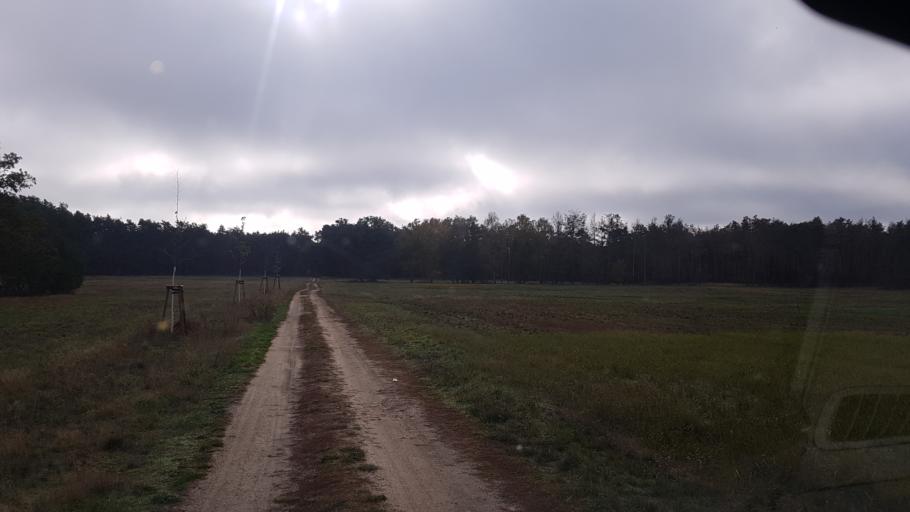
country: DE
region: Brandenburg
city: Schonborn
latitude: 51.6653
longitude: 13.4712
